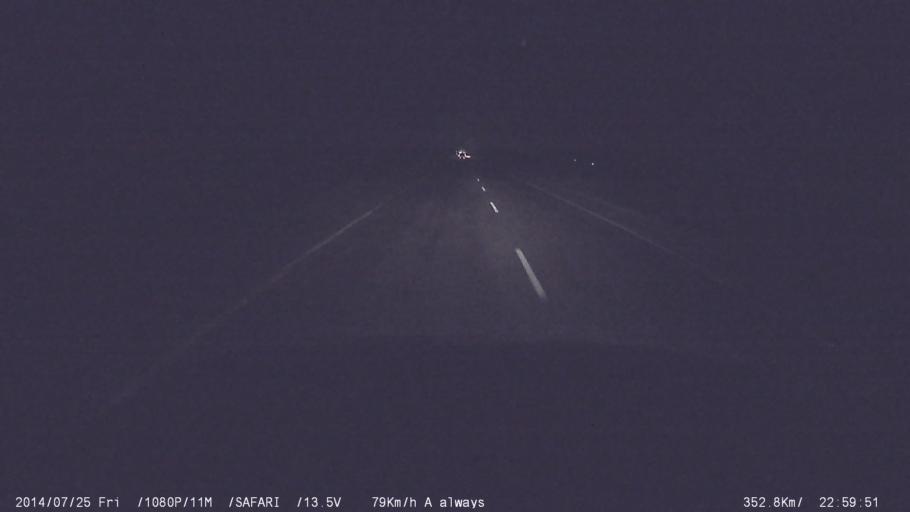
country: IN
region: Tamil Nadu
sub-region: Coimbatore
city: Singanallur
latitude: 10.9561
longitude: 77.0232
